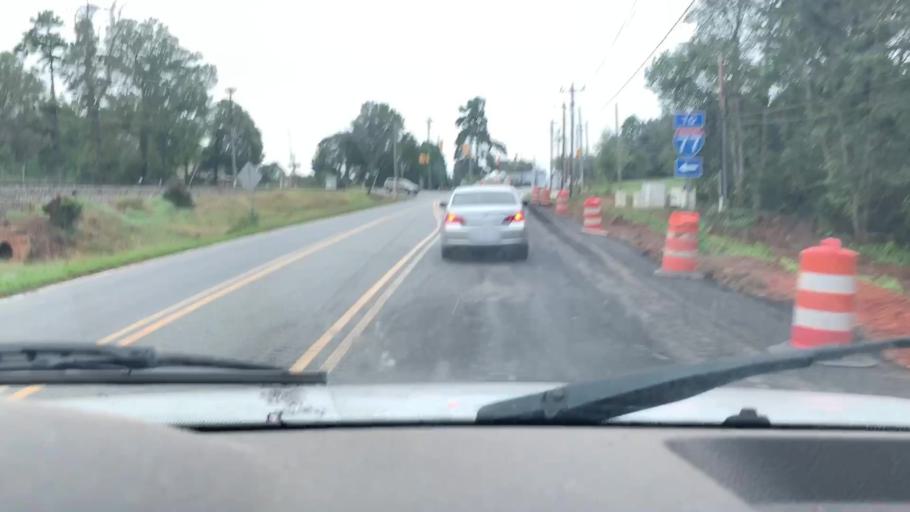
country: US
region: North Carolina
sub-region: Gaston County
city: Davidson
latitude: 35.5382
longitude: -80.8478
